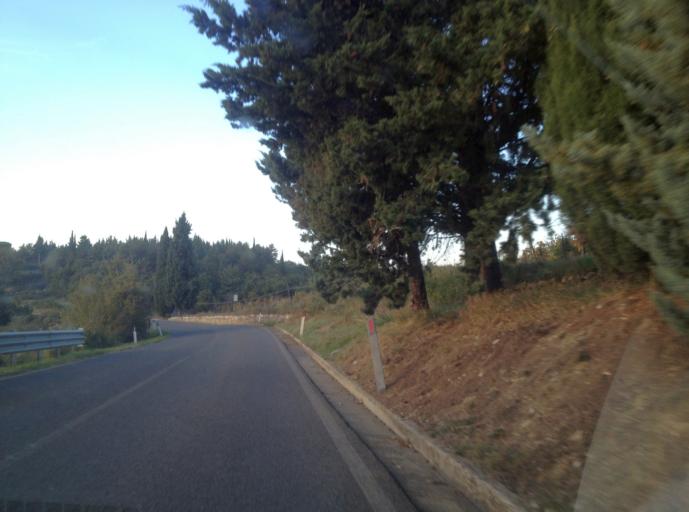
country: IT
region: Tuscany
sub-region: Provincia di Siena
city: Castellina in Chianti
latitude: 43.4486
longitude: 11.2950
